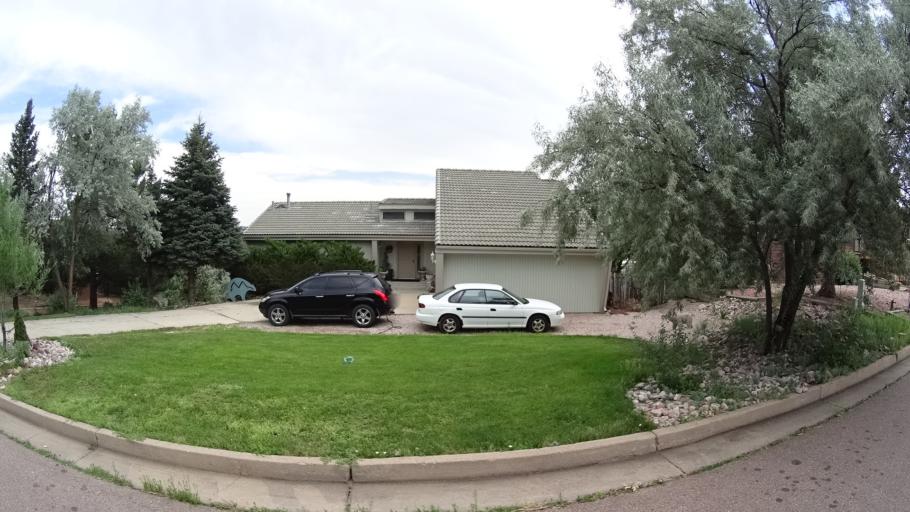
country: US
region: Colorado
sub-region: El Paso County
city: Colorado Springs
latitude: 38.9038
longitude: -104.8323
